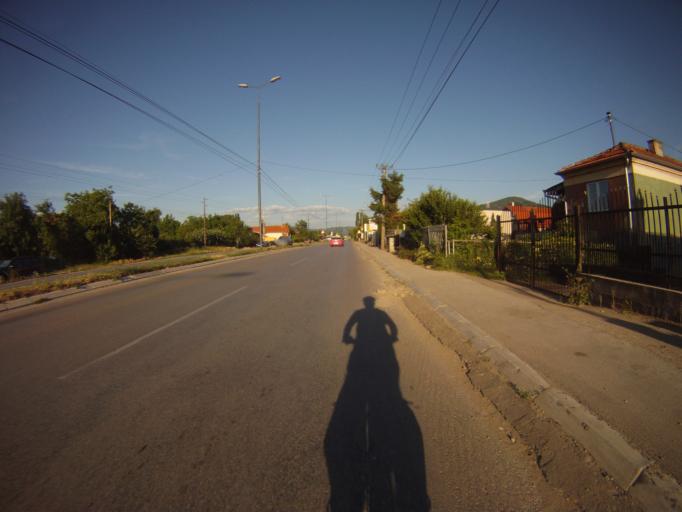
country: RS
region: Central Serbia
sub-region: Nisavski Okrug
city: Niska Banja
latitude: 43.3034
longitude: 21.9772
